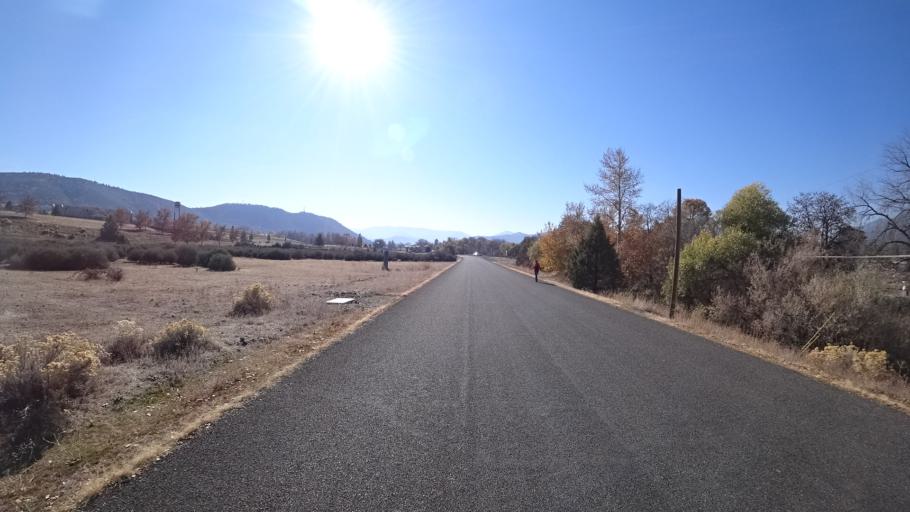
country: US
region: California
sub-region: Siskiyou County
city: Yreka
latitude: 41.7419
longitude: -122.6288
